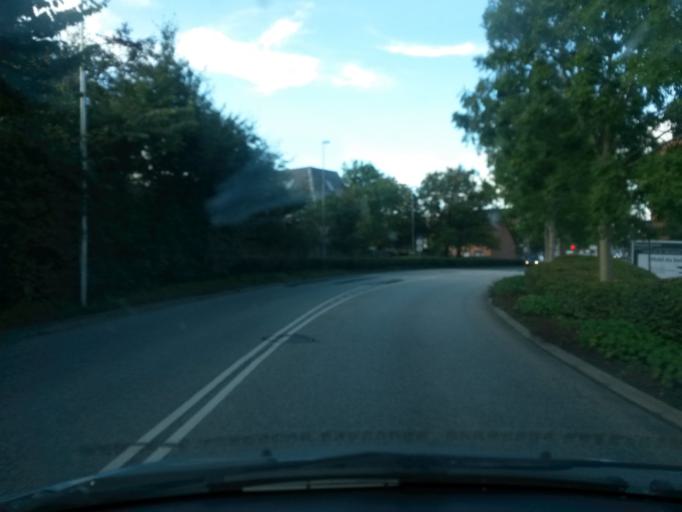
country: DK
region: Central Jutland
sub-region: Holstebro Kommune
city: Holstebro
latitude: 56.3546
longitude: 8.6158
